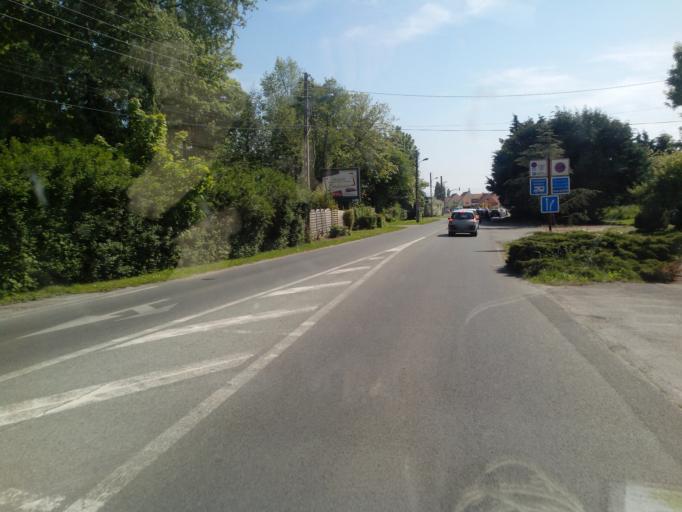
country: FR
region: Nord-Pas-de-Calais
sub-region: Departement du Pas-de-Calais
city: Berck
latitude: 50.4158
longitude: 1.5944
